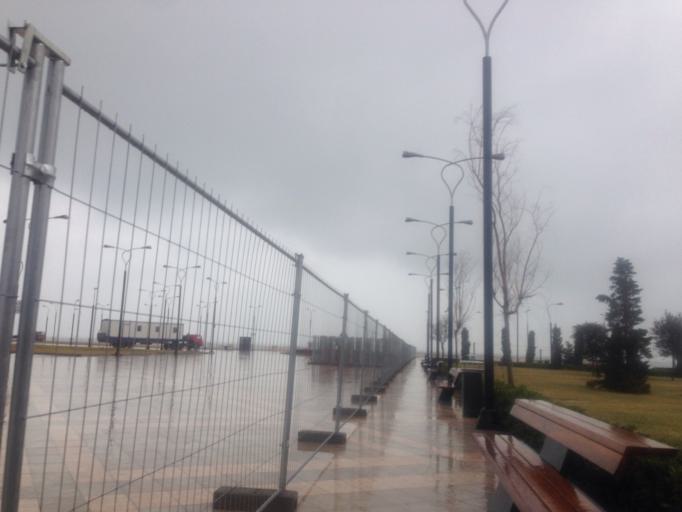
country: AZ
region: Baki
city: Badamdar
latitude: 40.3438
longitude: 49.8482
